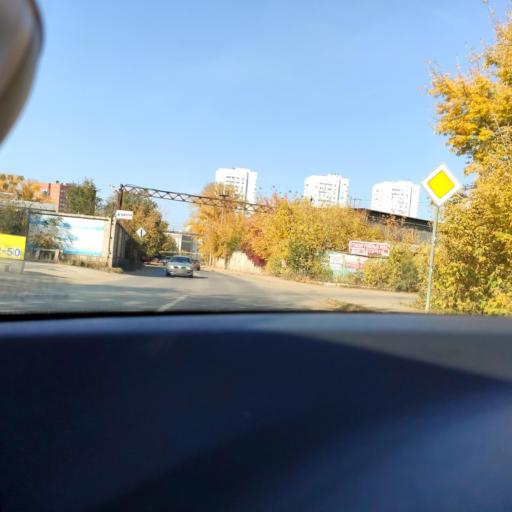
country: RU
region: Samara
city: Samara
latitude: 53.2180
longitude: 50.1968
